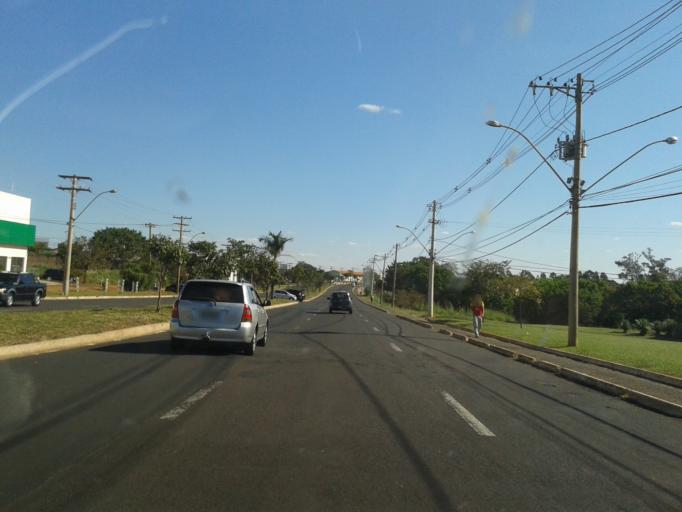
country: BR
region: Minas Gerais
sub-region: Uberaba
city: Uberaba
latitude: -19.7473
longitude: -47.9683
